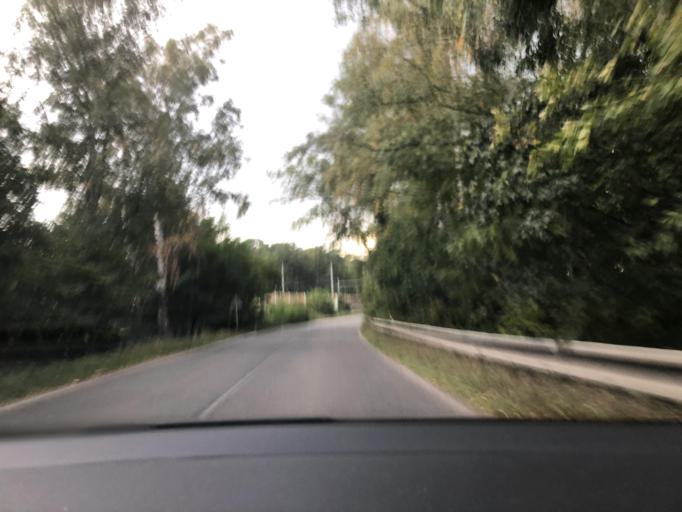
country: CZ
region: Central Bohemia
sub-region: Okres Kolin
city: Tynec nad Labem
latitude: 50.0404
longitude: 15.3635
